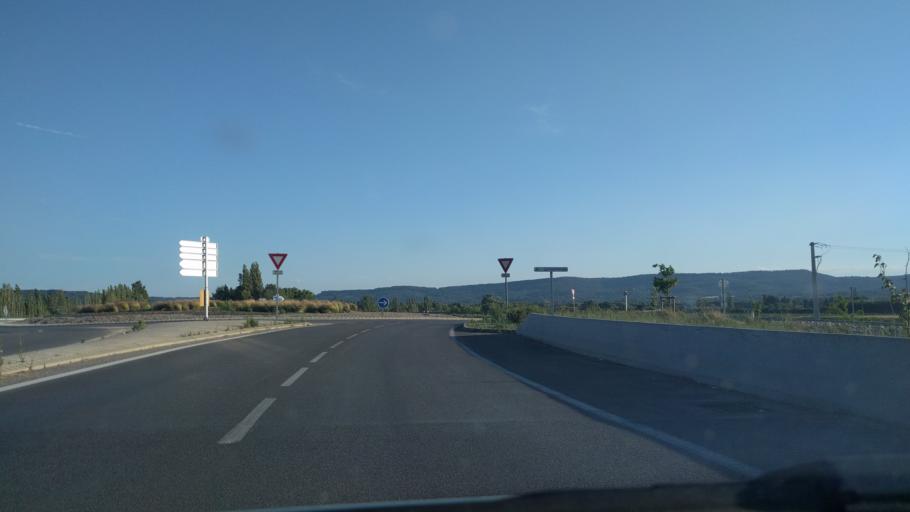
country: FR
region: Provence-Alpes-Cote d'Azur
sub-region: Departement du Vaucluse
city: Pertuis
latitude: 43.6636
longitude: 5.4949
